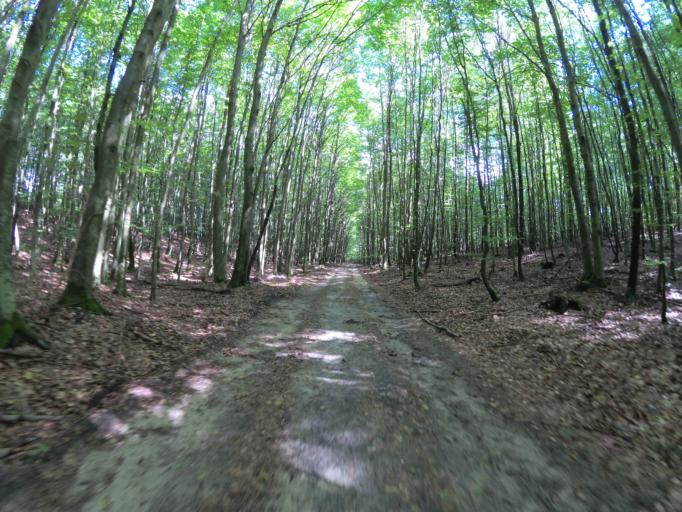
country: PL
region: Pomeranian Voivodeship
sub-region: Gdynia
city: Wielki Kack
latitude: 54.5086
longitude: 18.4489
